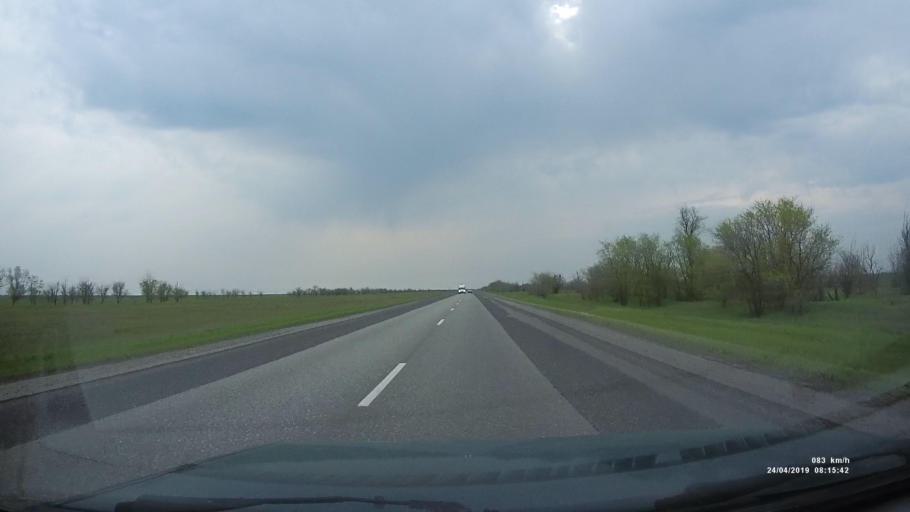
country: RU
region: Kalmykiya
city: Priyutnoye
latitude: 46.0998
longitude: 43.5990
